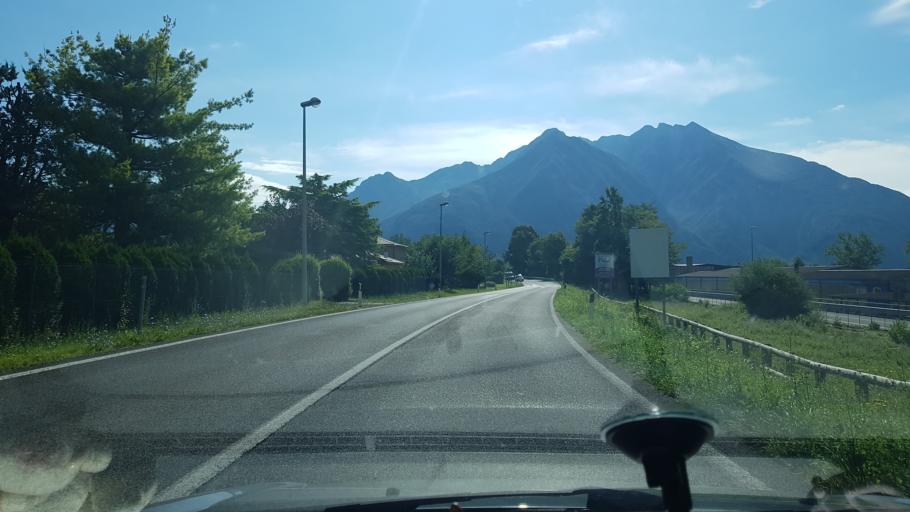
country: IT
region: Friuli Venezia Giulia
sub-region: Provincia di Udine
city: Amaro
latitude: 46.3716
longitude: 13.0862
